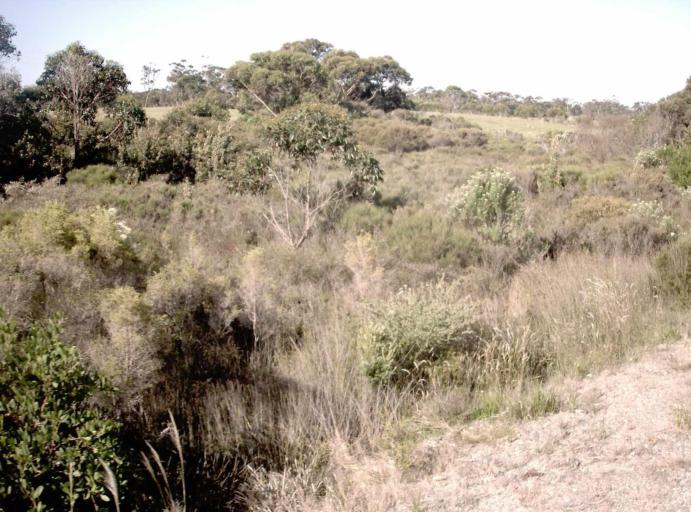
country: AU
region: Victoria
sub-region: East Gippsland
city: Lakes Entrance
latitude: -37.8010
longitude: 148.6428
